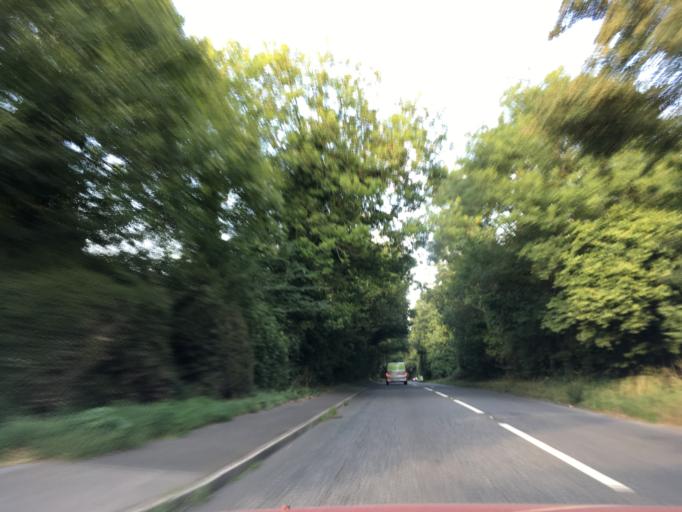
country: GB
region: England
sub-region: Gloucestershire
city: Bourton on the Water
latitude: 51.8825
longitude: -1.7749
